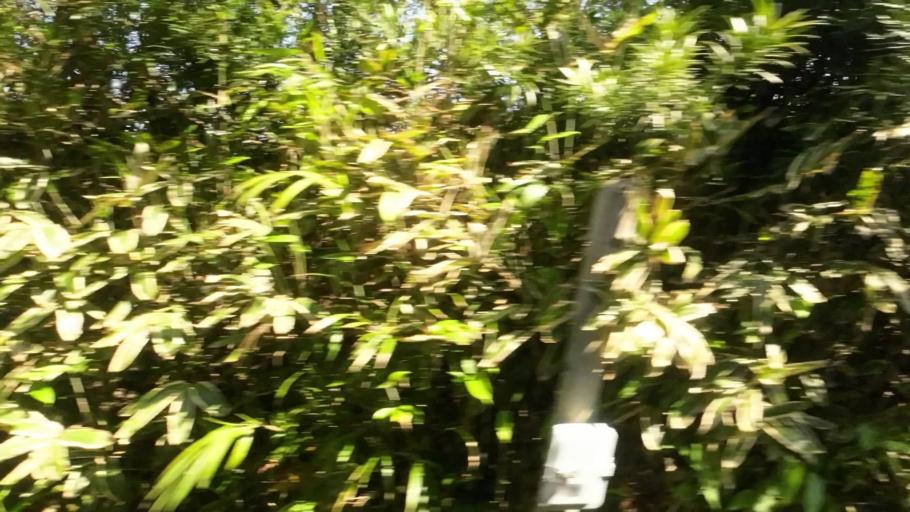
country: JP
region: Ehime
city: Niihama
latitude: 33.9735
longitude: 133.3448
